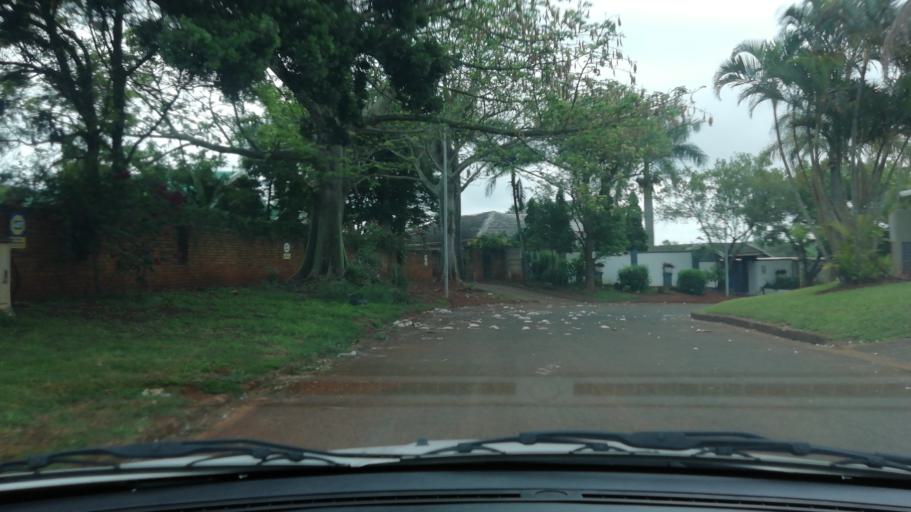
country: ZA
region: KwaZulu-Natal
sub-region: uThungulu District Municipality
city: Empangeni
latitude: -28.7653
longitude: 31.8963
